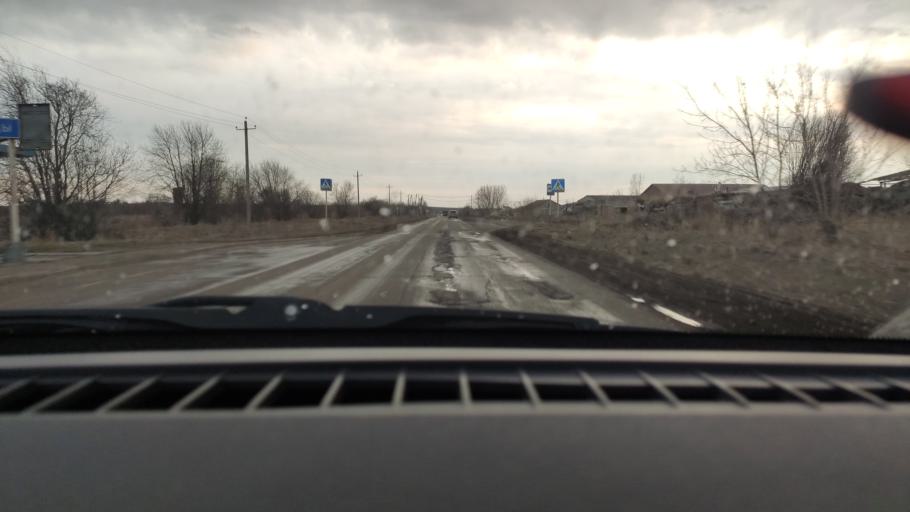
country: RU
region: Perm
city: Gamovo
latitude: 57.8952
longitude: 56.1165
